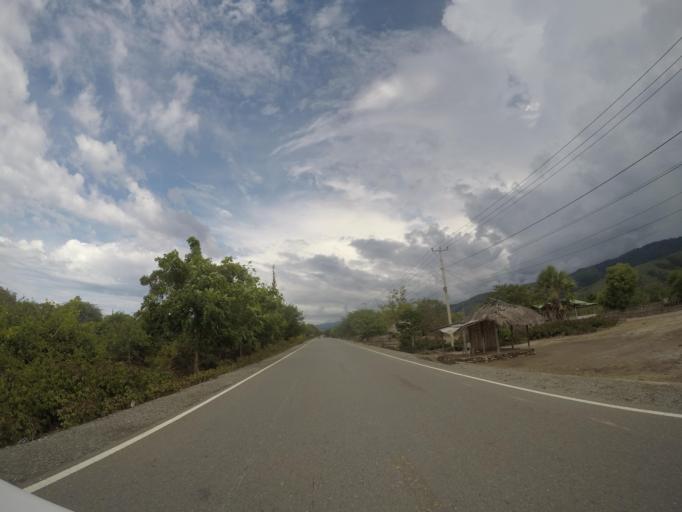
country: TL
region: Liquica
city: Maubara
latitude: -8.6061
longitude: 125.2238
